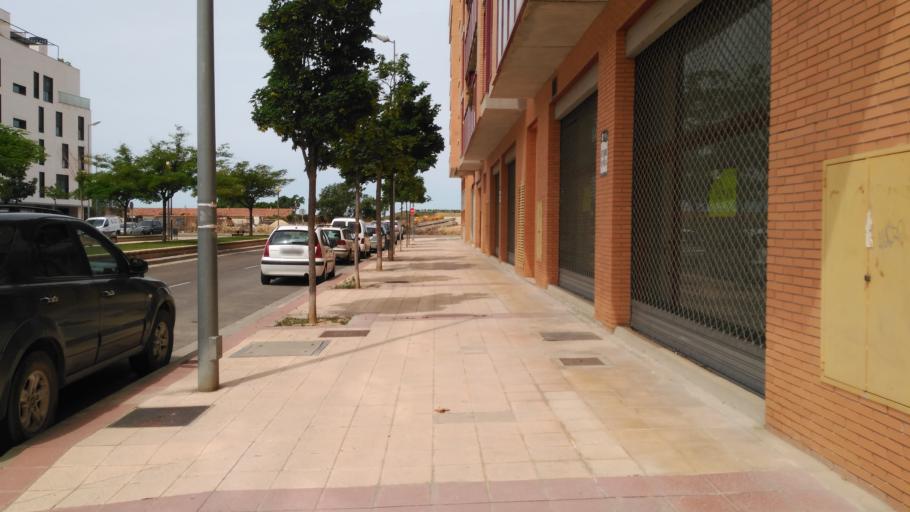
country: ES
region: Aragon
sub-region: Provincia de Huesca
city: Huesca
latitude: 42.1435
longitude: -0.4206
